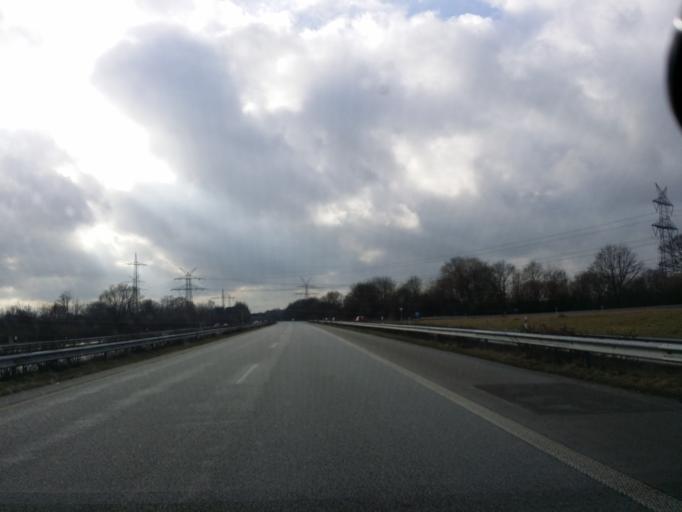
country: DE
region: Schleswig-Holstein
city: Schulldorf
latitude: 54.3050
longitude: 9.7523
